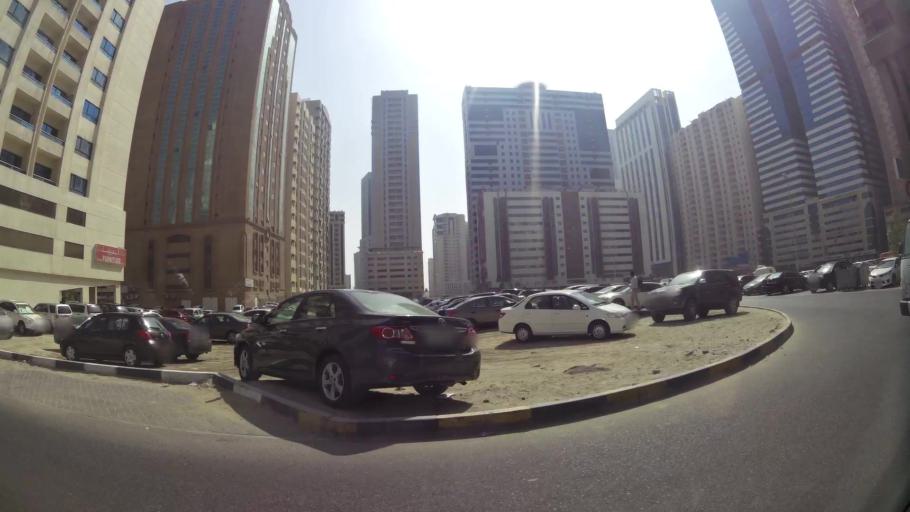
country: AE
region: Ash Shariqah
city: Sharjah
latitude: 25.3009
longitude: 55.3779
